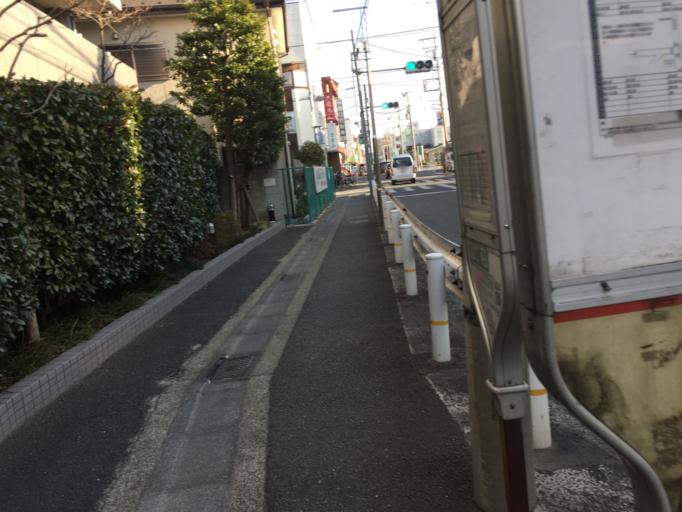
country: JP
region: Tokyo
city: Mitaka-shi
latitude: 35.6514
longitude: 139.6140
